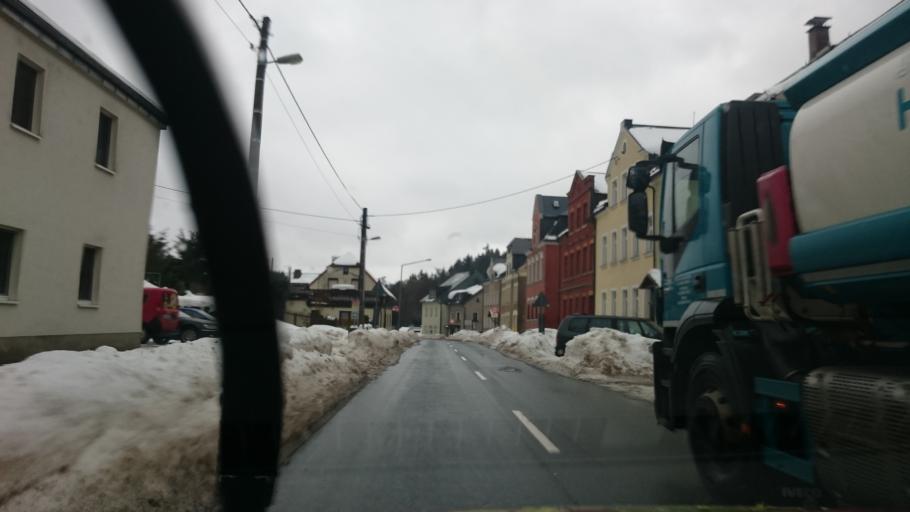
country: DE
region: Saxony
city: Zwota
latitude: 50.3532
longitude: 12.4310
